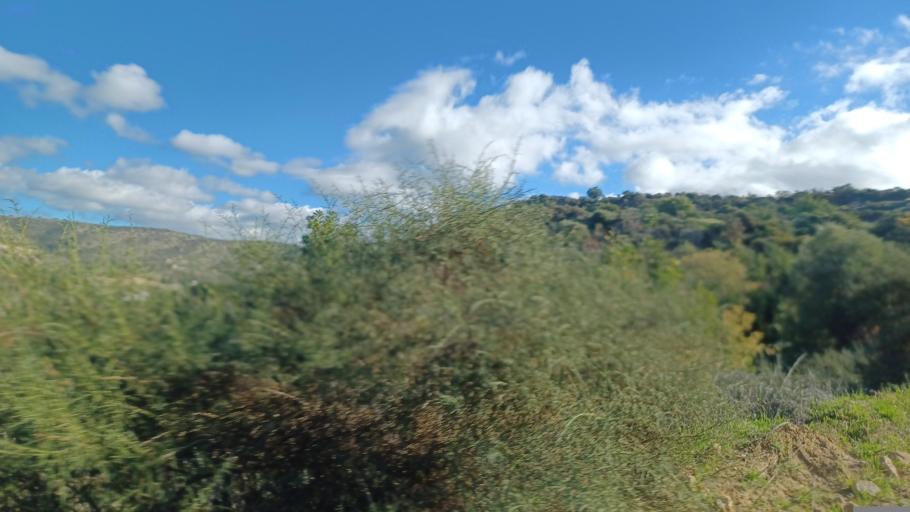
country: CY
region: Limassol
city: Pano Polemidia
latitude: 34.7594
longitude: 33.0075
